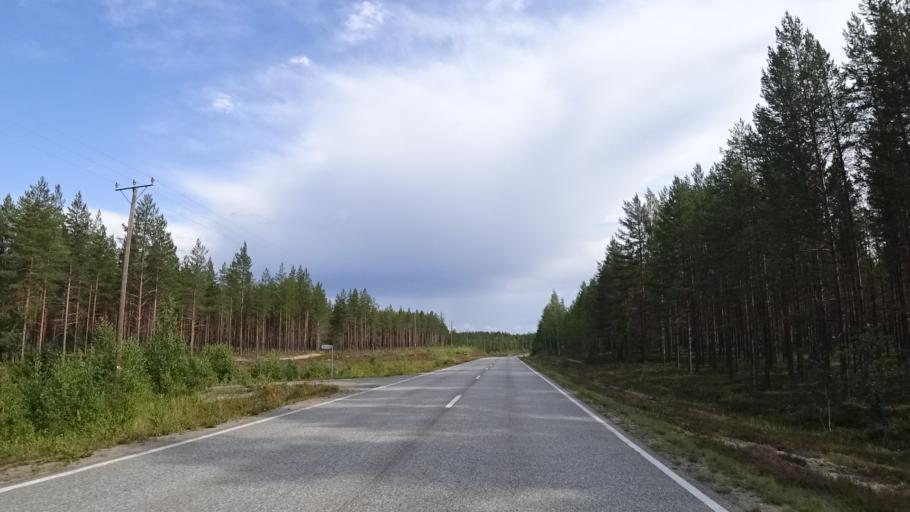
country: FI
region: North Karelia
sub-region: Joensuu
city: Ilomantsi
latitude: 62.6374
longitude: 31.0857
